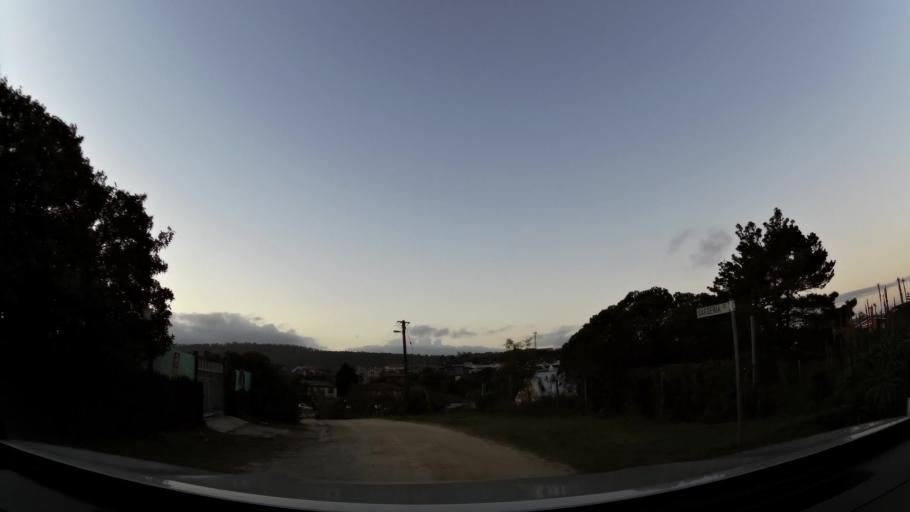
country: ZA
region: Western Cape
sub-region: Eden District Municipality
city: Knysna
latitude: -34.0283
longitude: 22.8080
